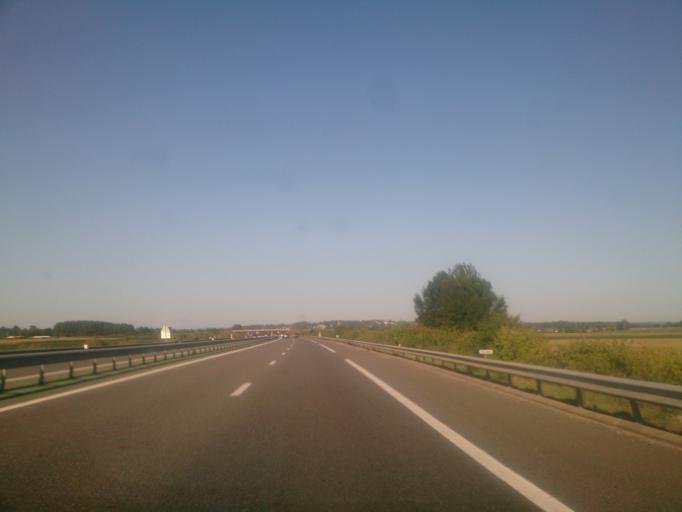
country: FR
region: Midi-Pyrenees
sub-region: Departement du Tarn-et-Garonne
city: Albias
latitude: 44.1025
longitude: 1.4522
